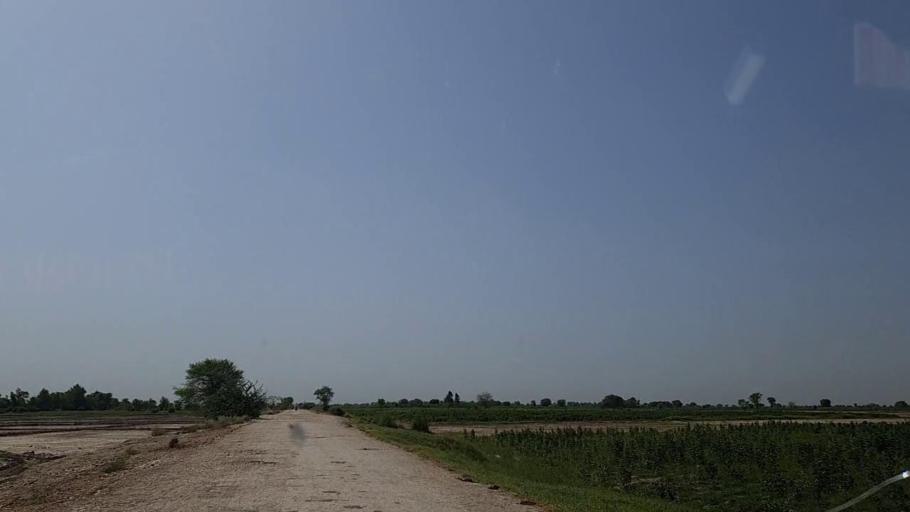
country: PK
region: Sindh
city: Naushahro Firoz
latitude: 26.8583
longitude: 68.0061
